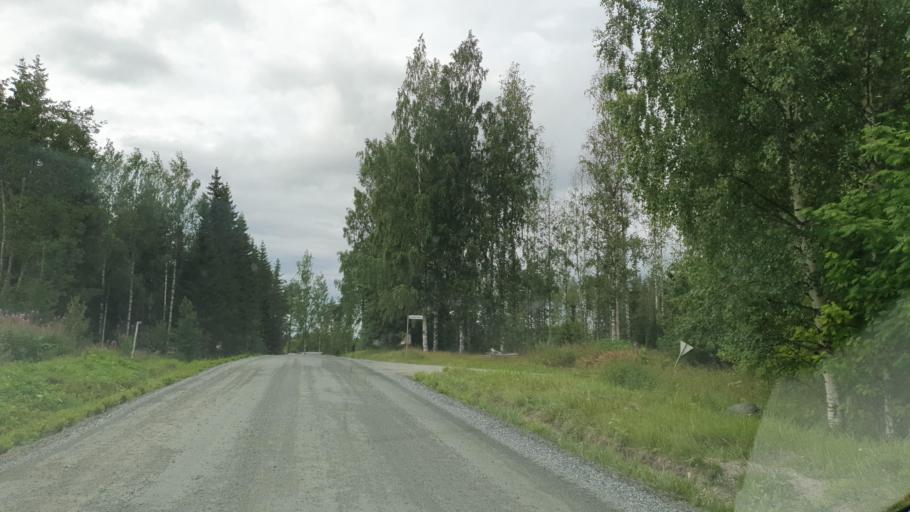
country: FI
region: Northern Savo
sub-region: Ylae-Savo
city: Iisalmi
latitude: 63.5179
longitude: 27.1035
